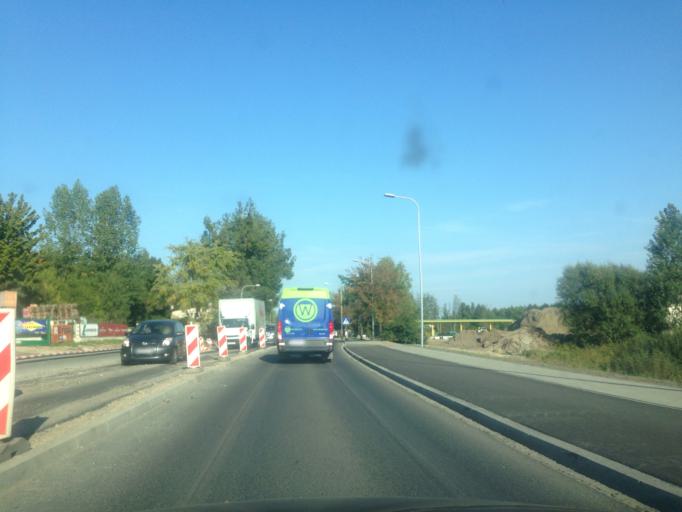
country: PL
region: Kujawsko-Pomorskie
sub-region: Powiat brodnicki
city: Brodnica
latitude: 53.2657
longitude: 19.4070
